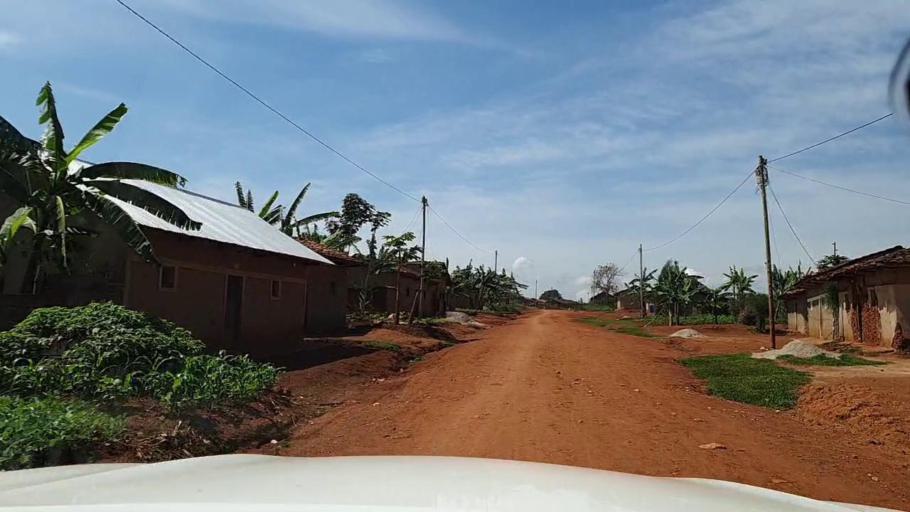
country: RW
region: Southern Province
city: Butare
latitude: -2.7187
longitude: 29.8383
